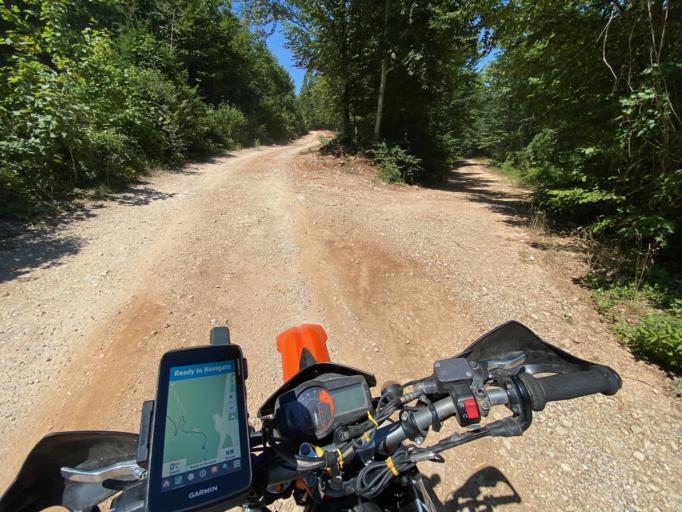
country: HR
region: Zadarska
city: Gracac
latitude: 44.2779
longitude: 15.7965
